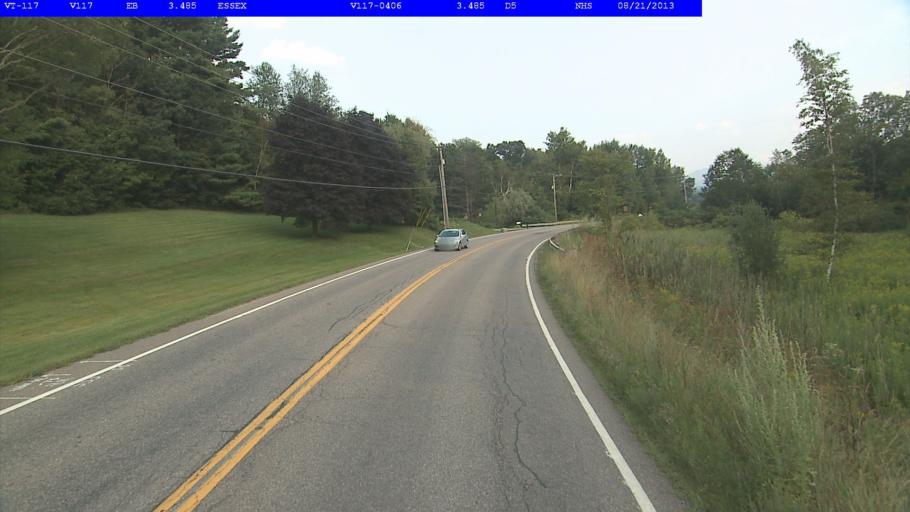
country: US
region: Vermont
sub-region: Chittenden County
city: Williston
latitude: 44.4788
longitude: -73.0452
